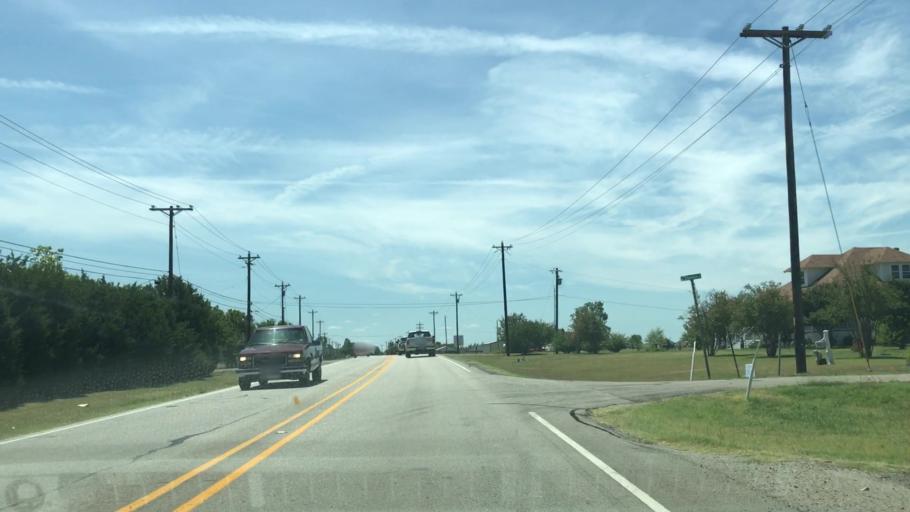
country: US
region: Texas
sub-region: Collin County
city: Saint Paul
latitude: 33.0422
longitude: -96.5502
